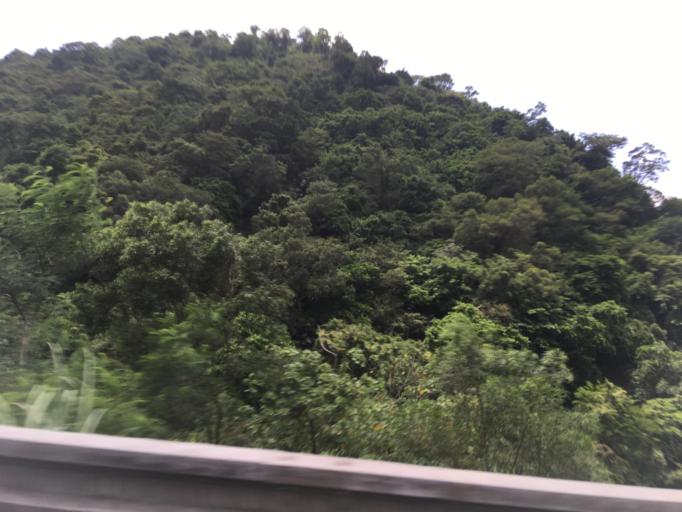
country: TW
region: Taiwan
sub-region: Yilan
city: Yilan
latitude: 24.6070
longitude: 121.7472
